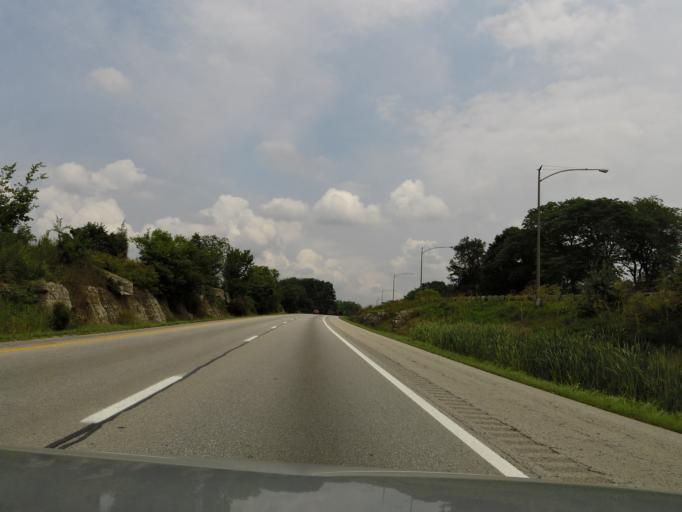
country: US
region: Kentucky
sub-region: Oldham County
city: Orchard Grass Hills
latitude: 38.3378
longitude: -85.5187
